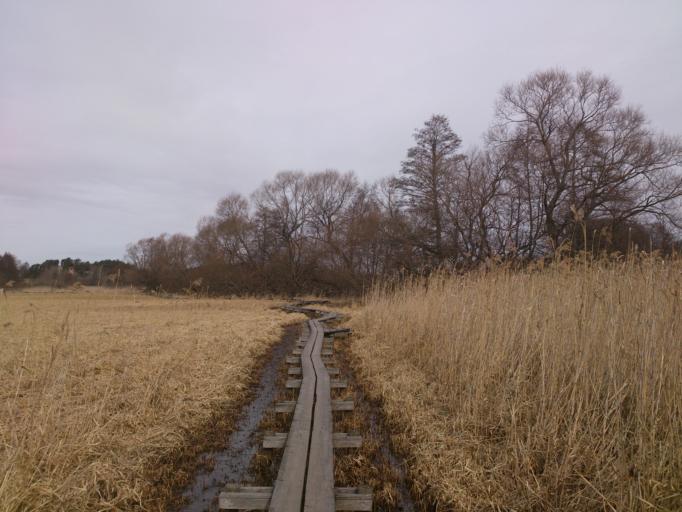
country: SE
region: Uppsala
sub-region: Uppsala Kommun
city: Saevja
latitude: 59.8031
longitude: 17.6673
